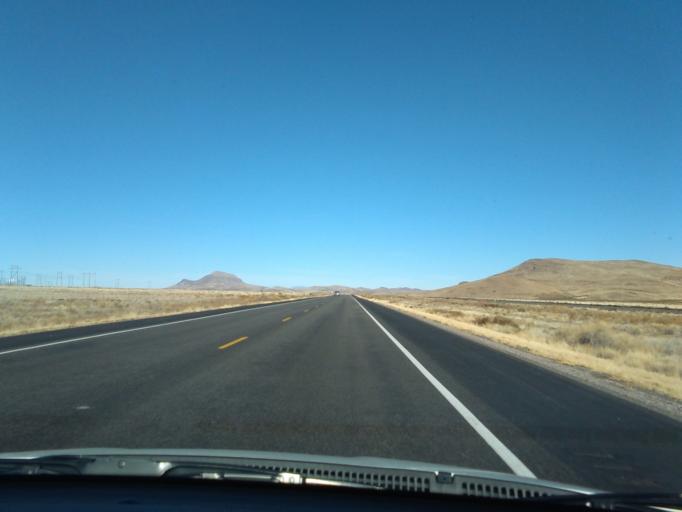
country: US
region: New Mexico
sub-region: Dona Ana County
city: Hatch
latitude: 32.5250
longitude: -107.4938
